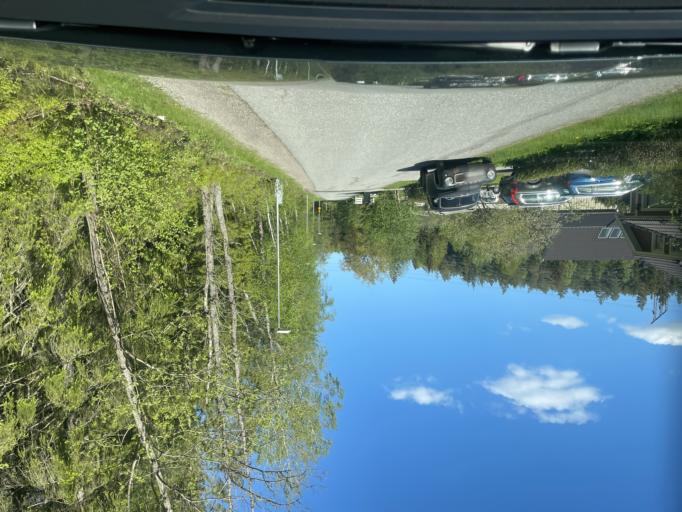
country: SE
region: Stockholm
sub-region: Botkyrka Kommun
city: Tullinge
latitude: 59.2263
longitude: 17.9033
